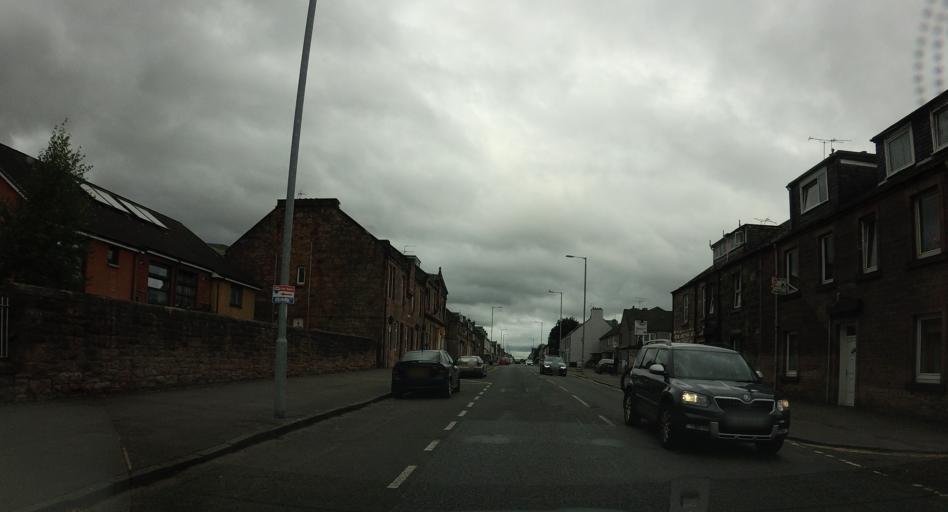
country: GB
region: Scotland
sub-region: Clackmannanshire
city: Alva
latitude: 56.1529
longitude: -3.8060
